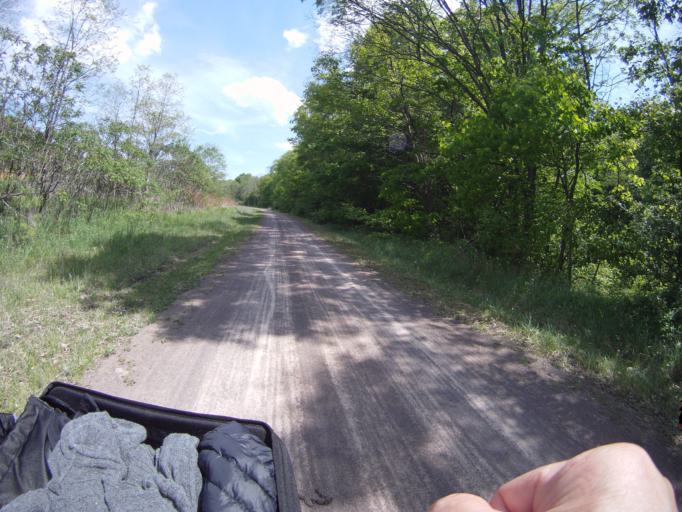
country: US
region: Pennsylvania
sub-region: Somerset County
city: Meyersdale
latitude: 39.7981
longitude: -78.9824
